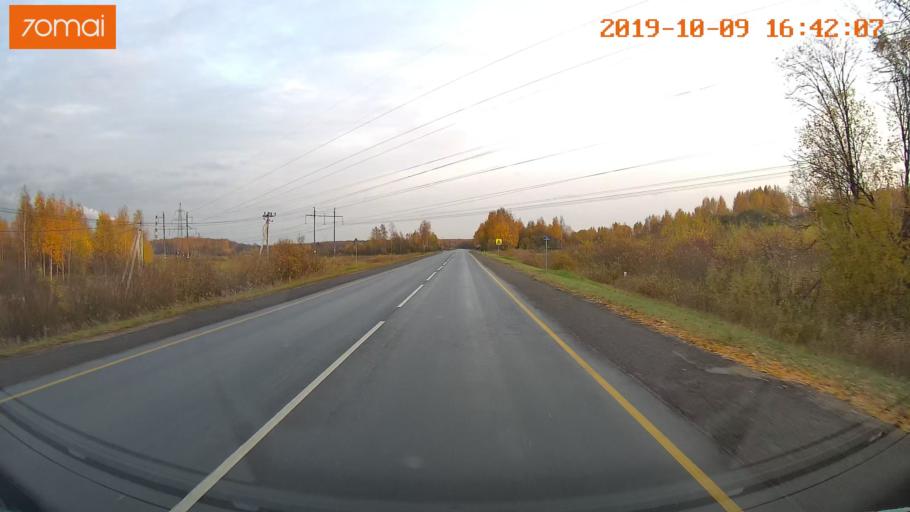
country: RU
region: Kostroma
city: Volgorechensk
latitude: 57.4656
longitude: 41.0941
